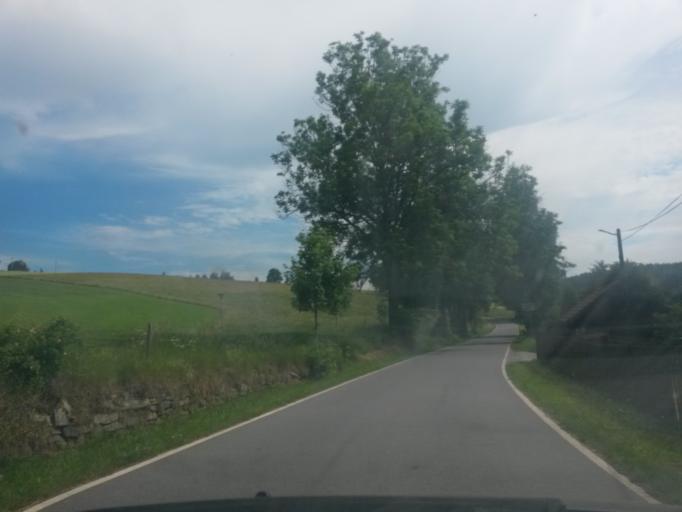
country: CZ
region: Vysocina
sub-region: Okres Zd'ar nad Sazavou
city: Jimramov
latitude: 49.6175
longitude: 16.2023
